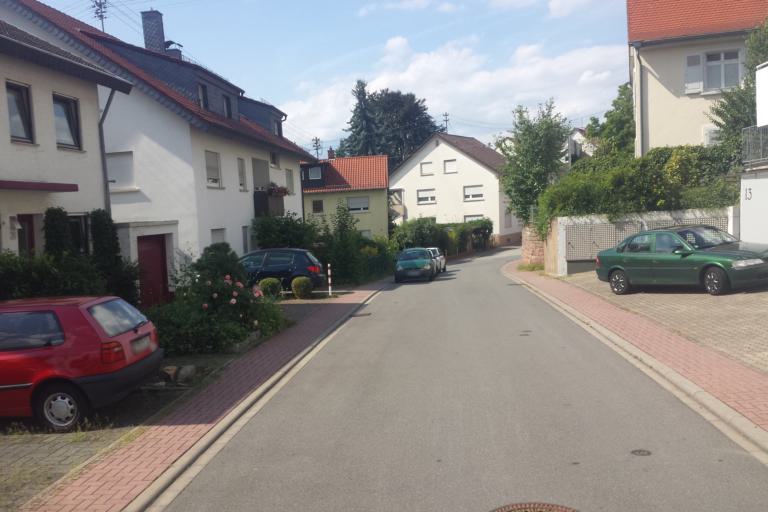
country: DE
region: Baden-Wuerttemberg
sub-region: Karlsruhe Region
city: Dossenheim
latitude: 49.4488
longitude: 8.6782
